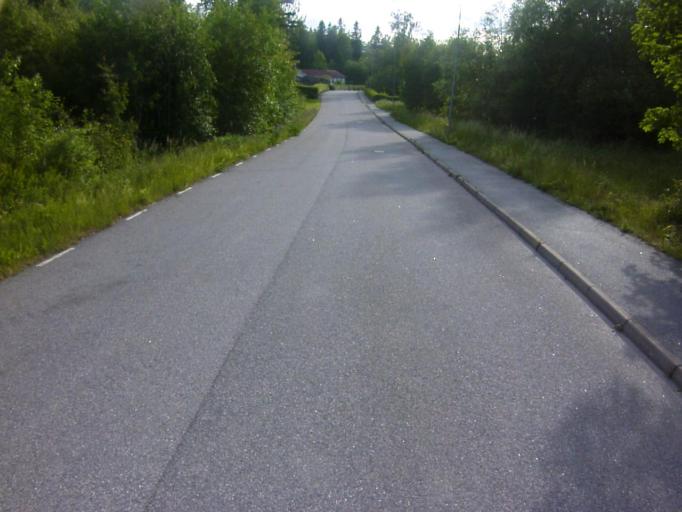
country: SE
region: Soedermanland
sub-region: Eskilstuna Kommun
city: Skogstorp
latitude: 59.3263
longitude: 16.4810
